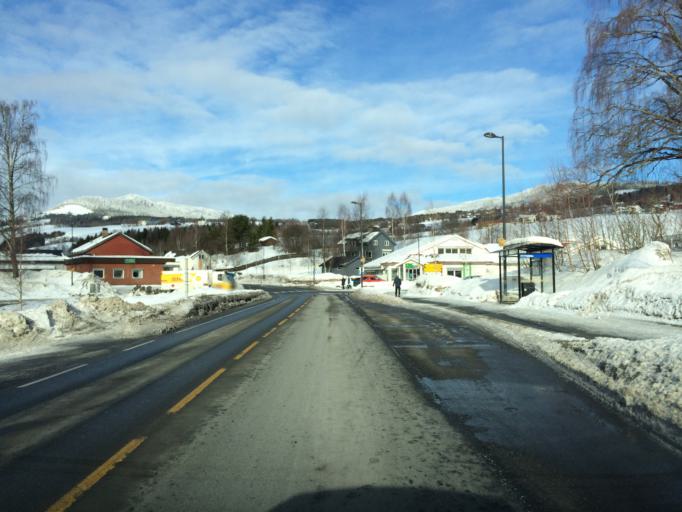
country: NO
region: Oppland
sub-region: Gausdal
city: Segalstad bru
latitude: 61.2152
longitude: 10.2857
